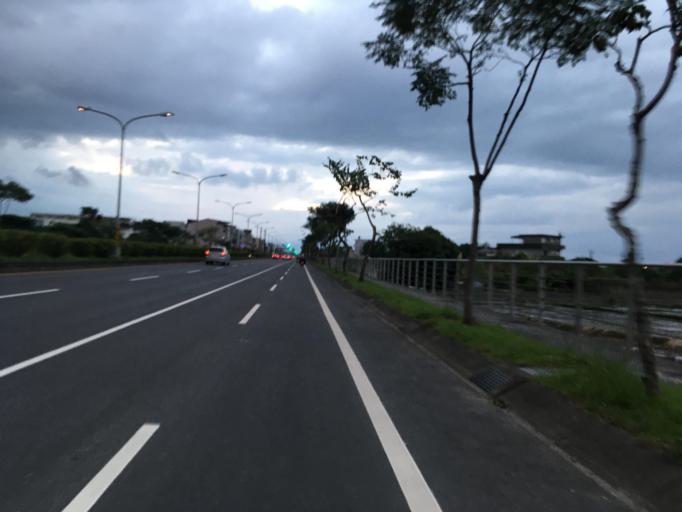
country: TW
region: Taiwan
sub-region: Yilan
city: Yilan
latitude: 24.6199
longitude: 121.8430
